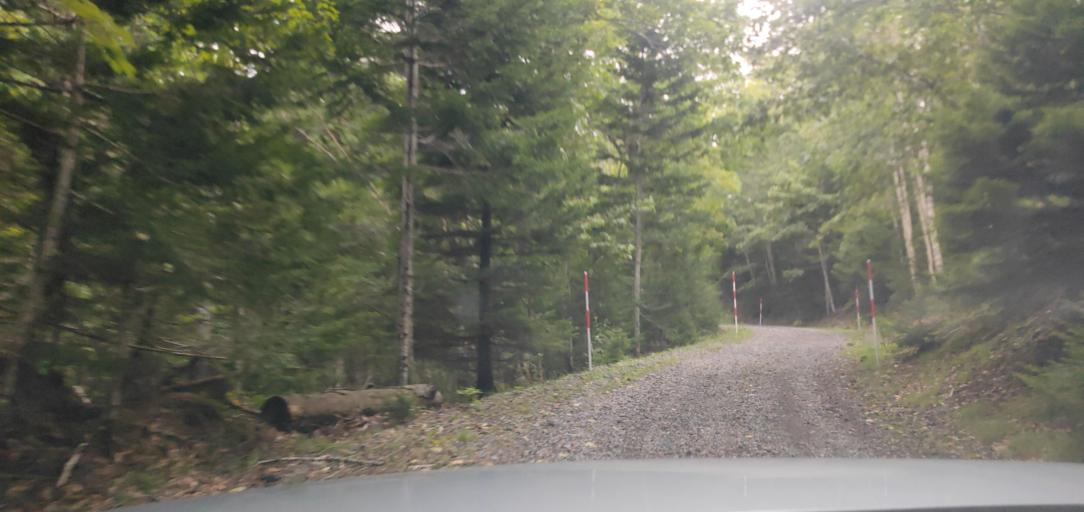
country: JP
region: Hokkaido
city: Kitami
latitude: 43.3698
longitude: 143.9493
